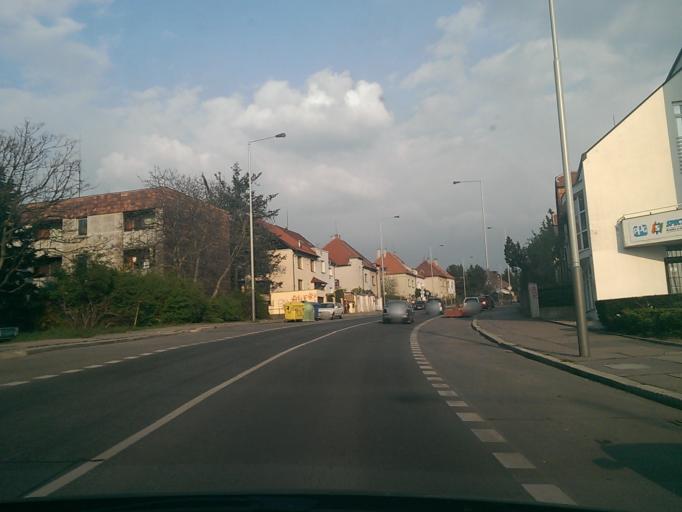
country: CZ
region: Praha
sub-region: Praha 14
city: Hostavice
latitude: 50.0521
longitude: 14.5328
